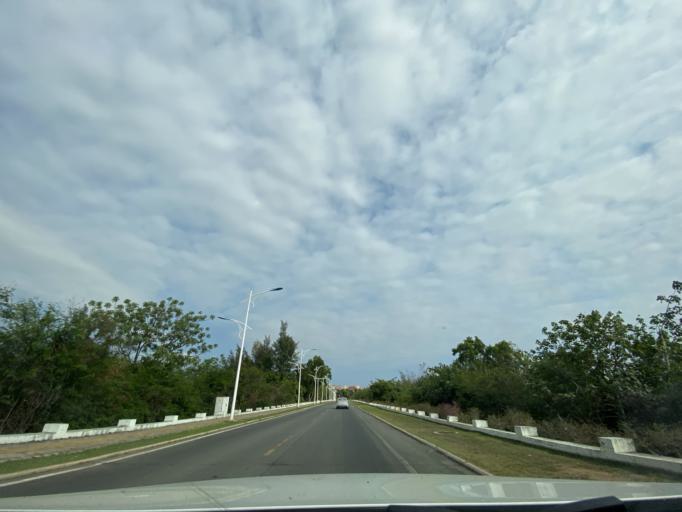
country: CN
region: Hainan
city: Tiandu
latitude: 18.2322
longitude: 109.6189
